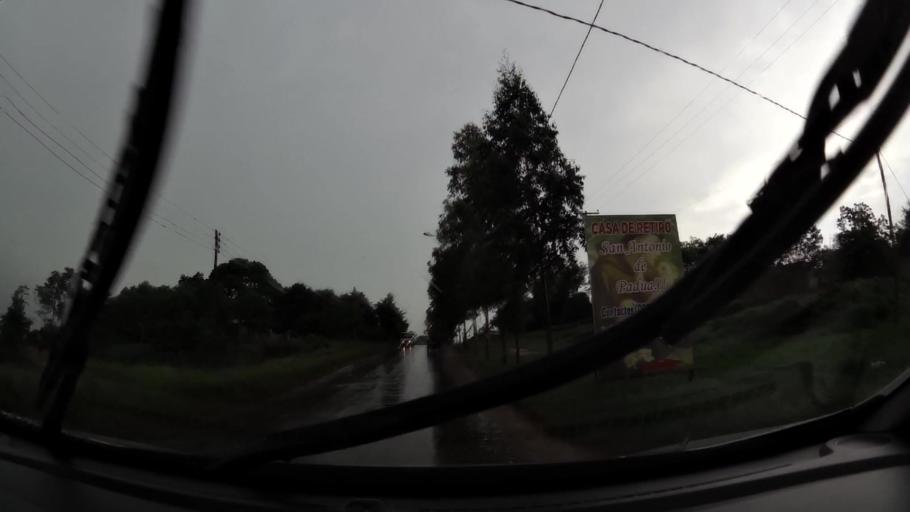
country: PY
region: Alto Parana
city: Presidente Franco
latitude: -25.5314
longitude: -54.6802
